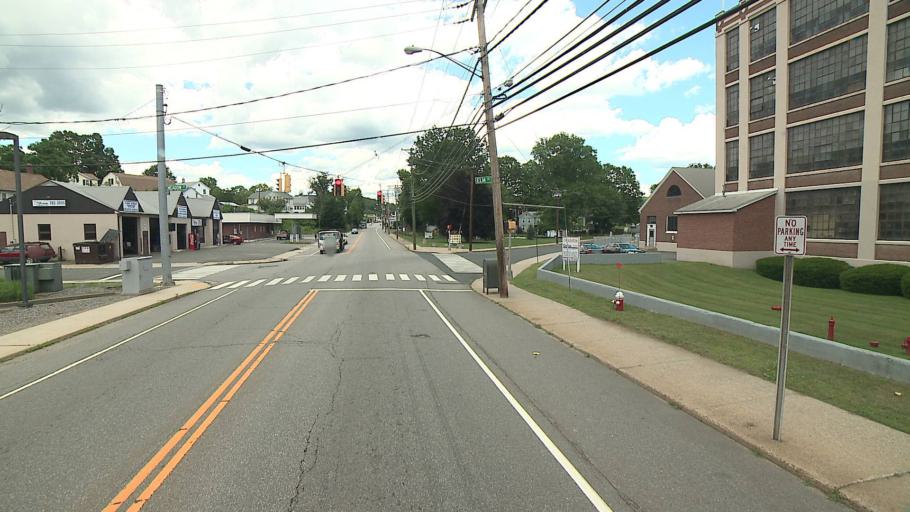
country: US
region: Connecticut
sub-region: Litchfield County
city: Thomaston
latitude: 41.6697
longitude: -73.0774
